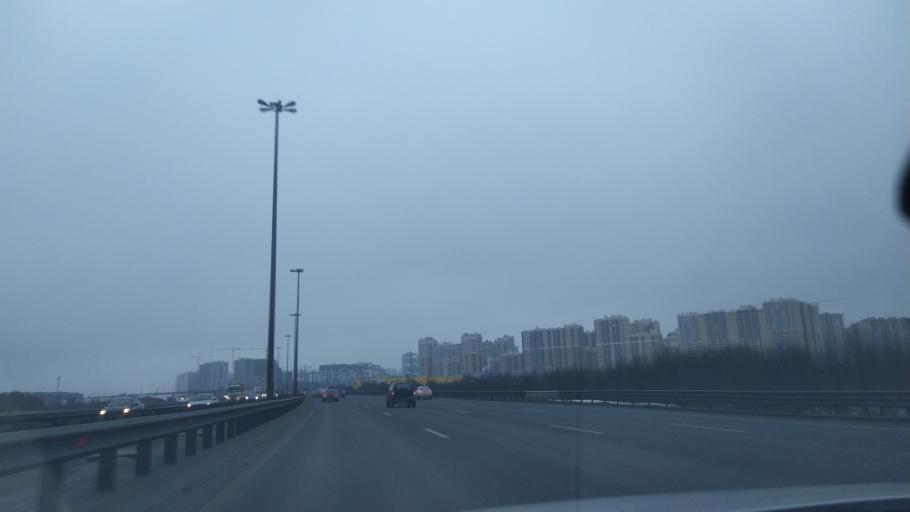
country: RU
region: St.-Petersburg
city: Krasnogvargeisky
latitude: 59.9228
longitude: 30.5283
